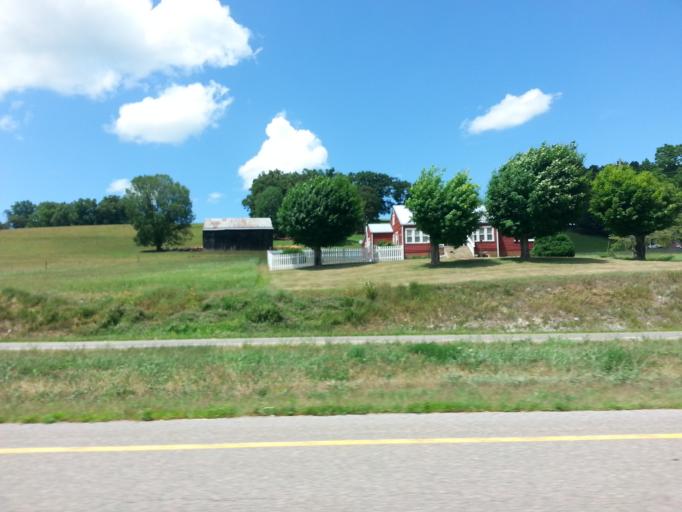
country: US
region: Virginia
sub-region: Lee County
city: Jonesville
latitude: 36.6815
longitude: -83.1496
